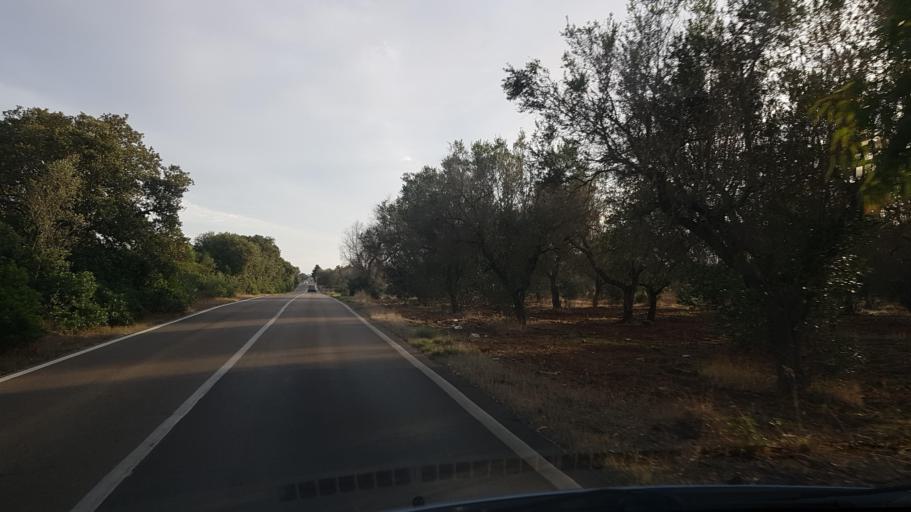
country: IT
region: Apulia
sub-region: Provincia di Brindisi
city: Torchiarolo
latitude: 40.4787
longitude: 18.1244
